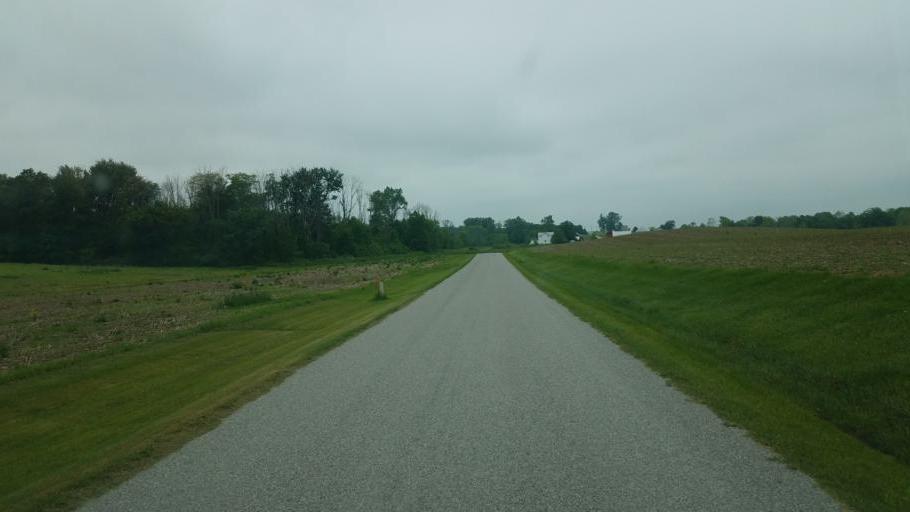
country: US
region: Ohio
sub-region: Knox County
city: Centerburg
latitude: 40.3974
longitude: -82.7320
